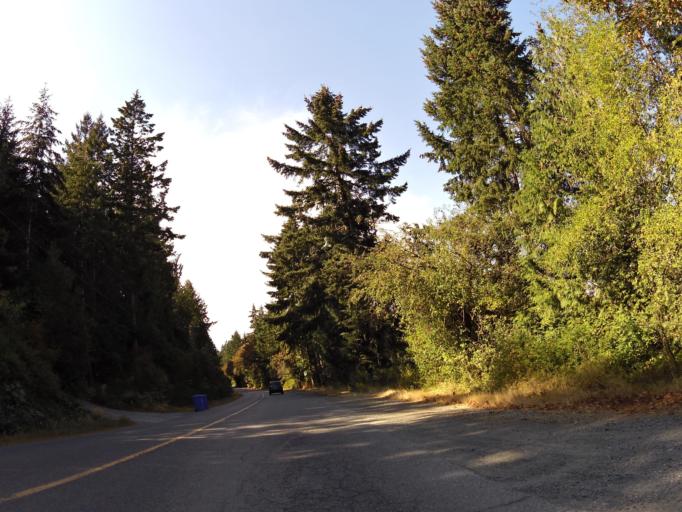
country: CA
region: British Columbia
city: North Saanich
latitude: 48.6902
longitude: -123.5573
